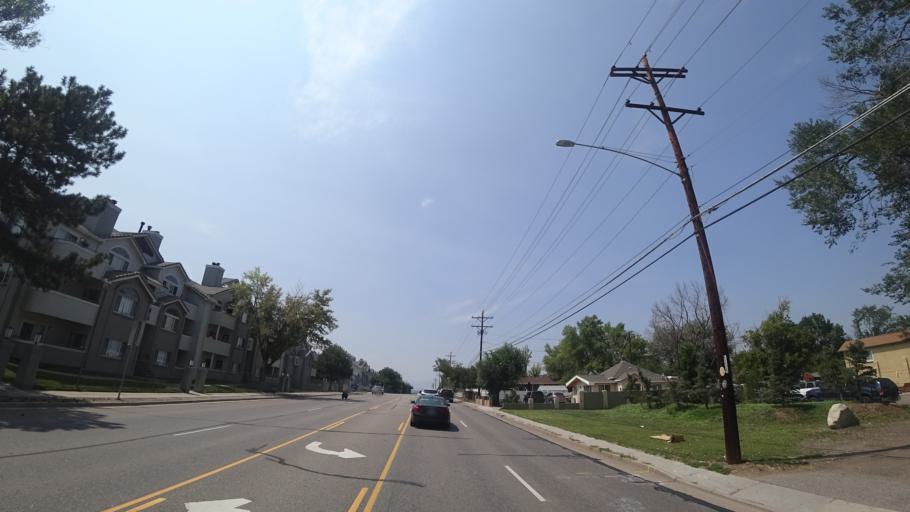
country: US
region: Colorado
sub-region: Arapahoe County
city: Englewood
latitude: 39.6241
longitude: -104.9915
